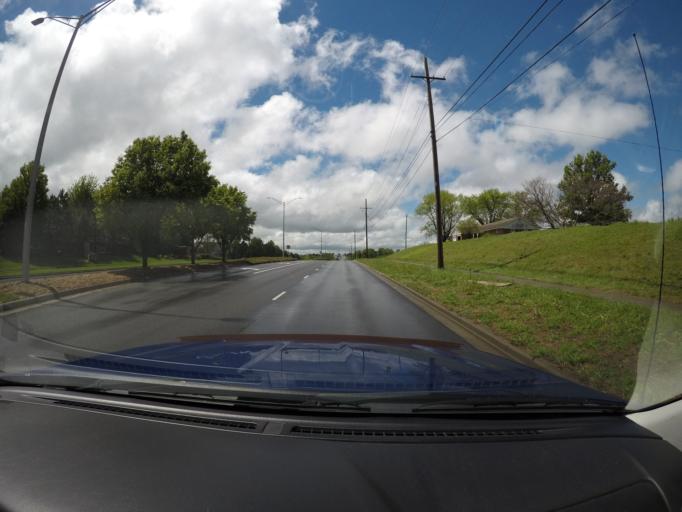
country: US
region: Kansas
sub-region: Johnson County
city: Olathe
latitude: 38.9274
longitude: -94.8442
